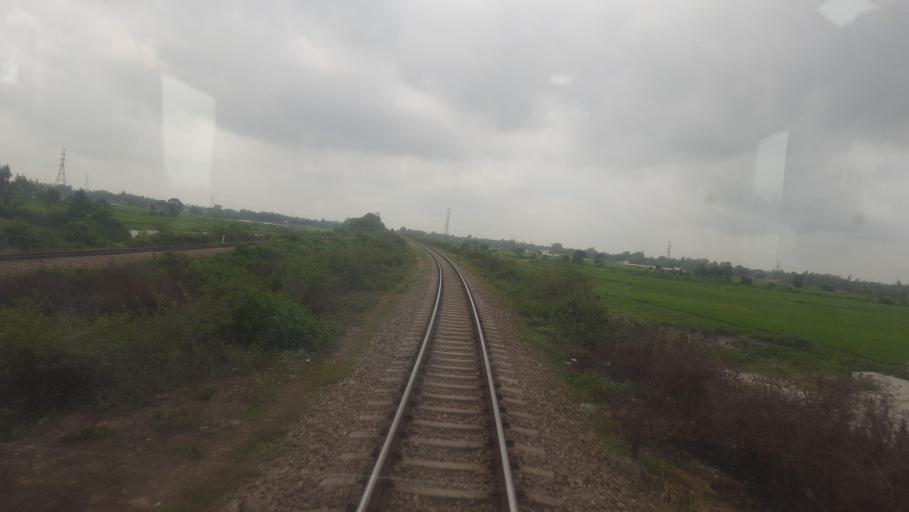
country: BD
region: Dhaka
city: Bhairab Bazar
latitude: 24.0476
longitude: 90.9676
